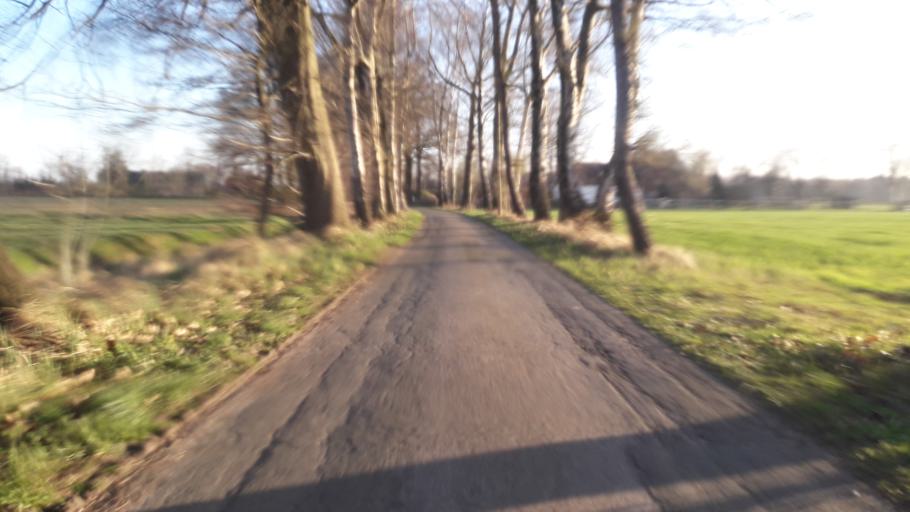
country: DE
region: North Rhine-Westphalia
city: Rietberg
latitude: 51.7871
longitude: 8.4547
